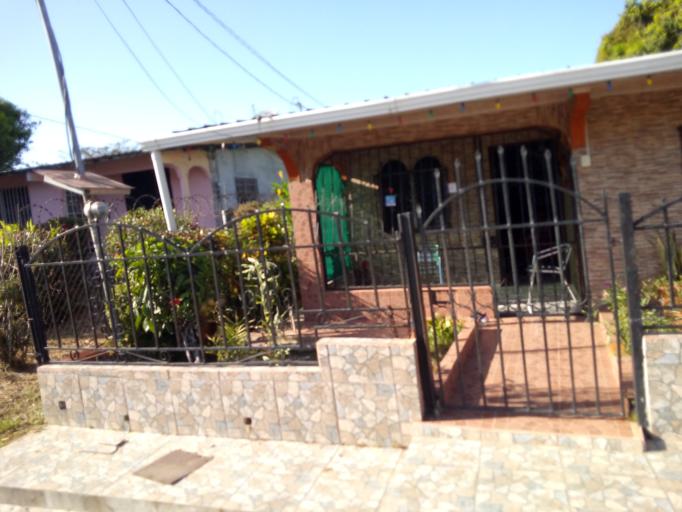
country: PA
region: Veraguas
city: Santiago de Veraguas
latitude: 8.1080
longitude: -80.9696
